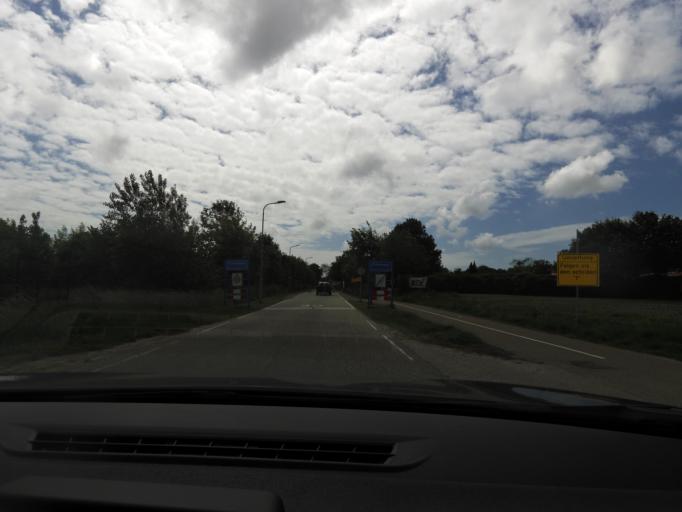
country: NL
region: Zeeland
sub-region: Schouwen-Duiveland
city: Scharendijke
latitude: 51.7311
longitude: 3.8184
